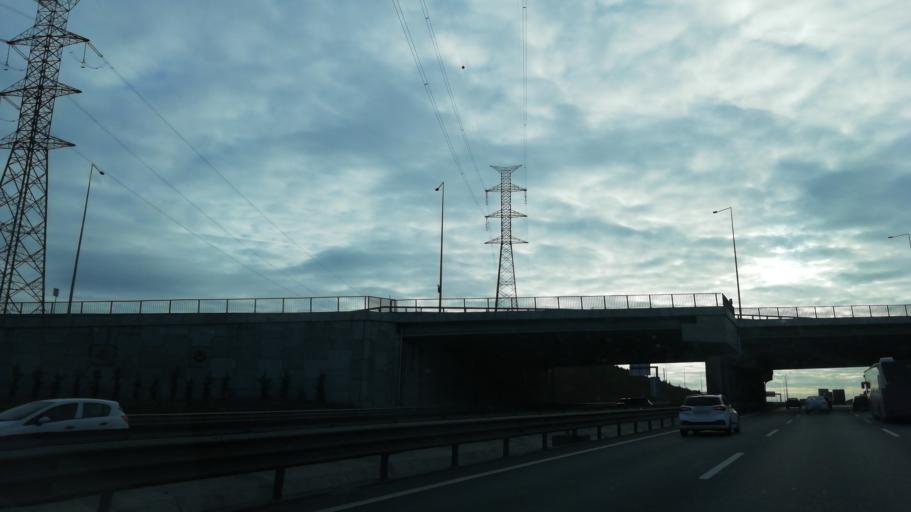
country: TR
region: Istanbul
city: Sultanbeyli
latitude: 40.9472
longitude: 29.3104
